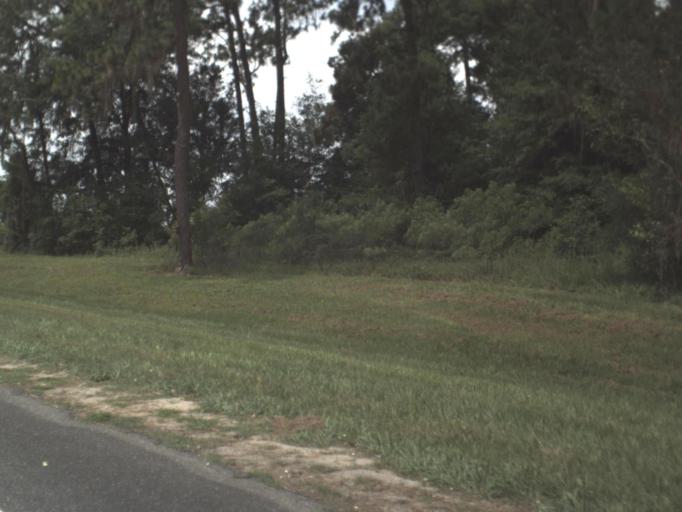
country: US
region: Florida
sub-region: Suwannee County
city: Live Oak
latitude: 30.2165
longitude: -82.9880
